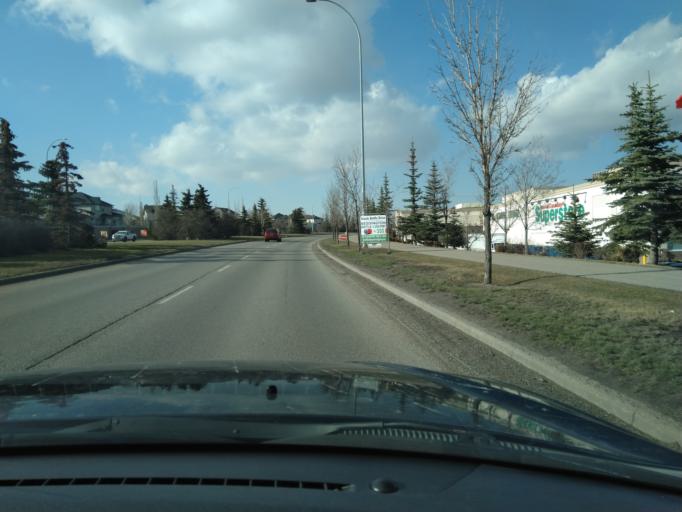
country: CA
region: Alberta
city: Calgary
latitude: 51.1613
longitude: -114.0708
